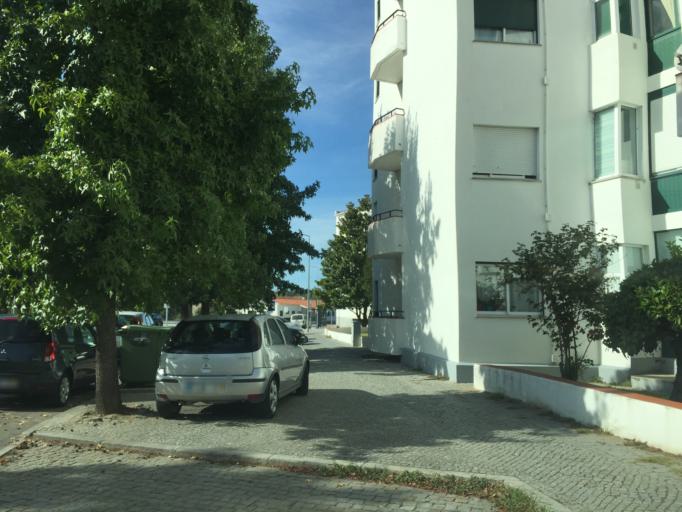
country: PT
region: Portalegre
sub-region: Portalegre
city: Portalegre
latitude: 39.3013
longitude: -7.4330
